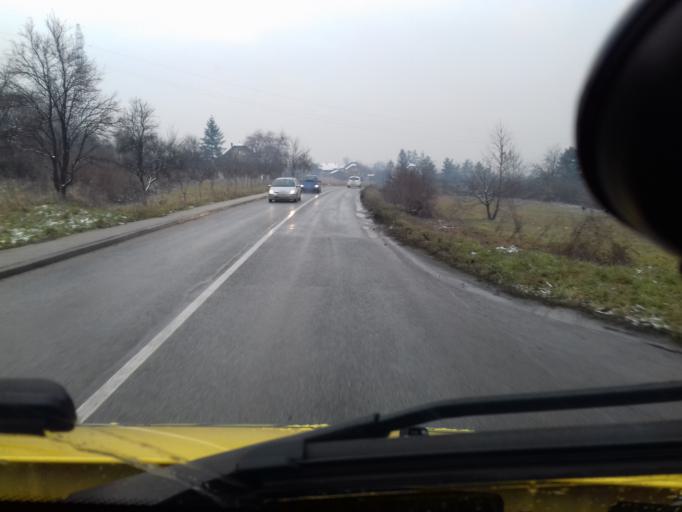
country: BA
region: Federation of Bosnia and Herzegovina
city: Zenica
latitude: 44.2145
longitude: 17.8910
